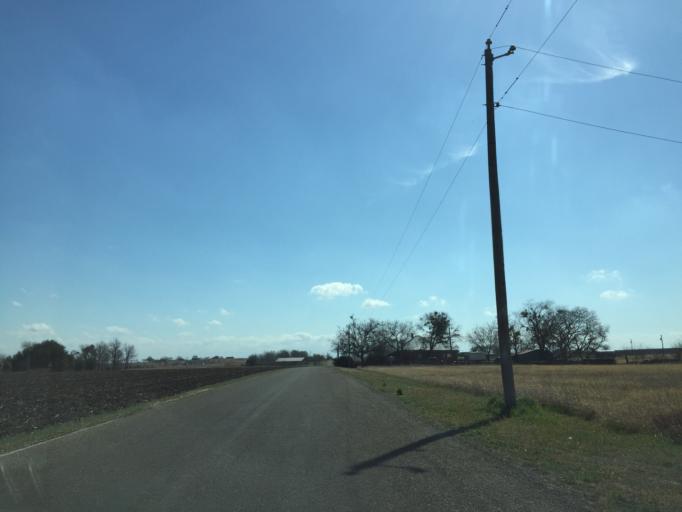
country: US
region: Texas
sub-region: Williamson County
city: Granger
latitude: 30.7558
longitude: -97.5090
